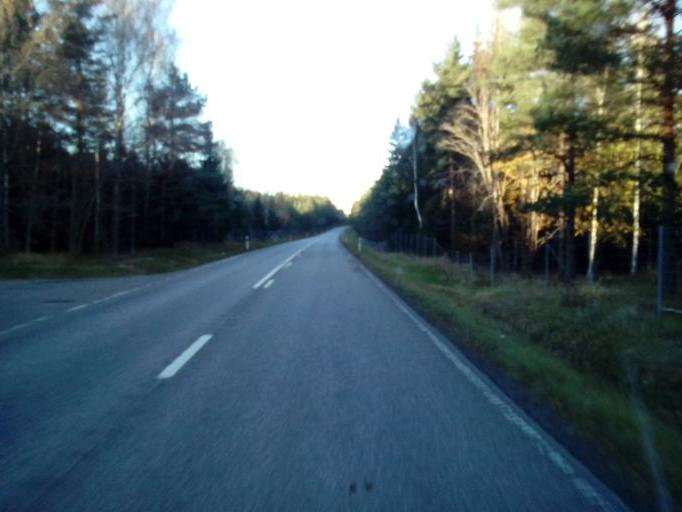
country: SE
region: OErebro
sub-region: Hallsbergs Kommun
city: Palsboda
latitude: 58.9287
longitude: 15.4304
